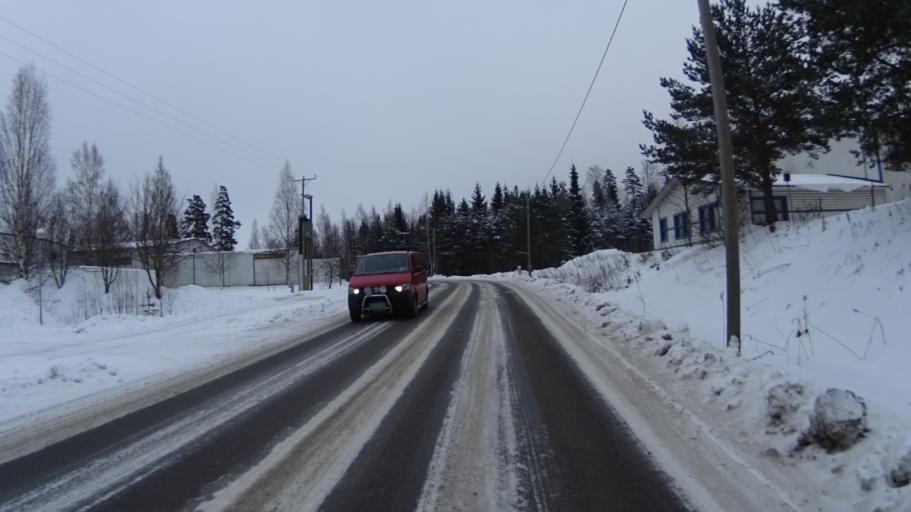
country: FI
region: Uusimaa
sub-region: Helsinki
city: Karkkila
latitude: 60.5182
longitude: 24.2417
